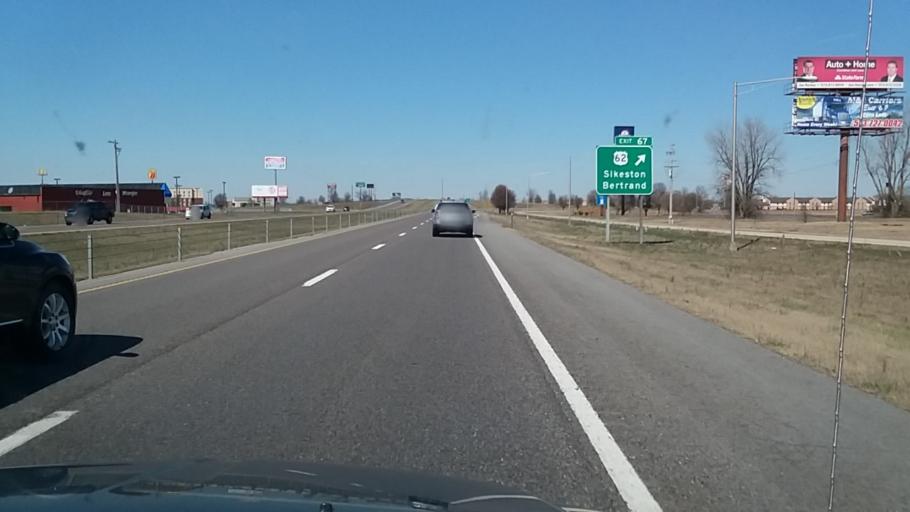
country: US
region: Missouri
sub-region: Scott County
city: Sikeston
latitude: 36.8866
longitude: -89.5331
